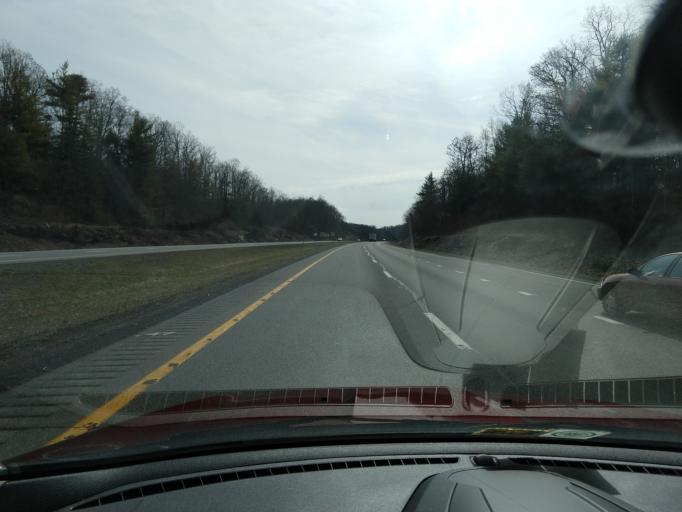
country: US
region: West Virginia
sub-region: Greenbrier County
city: Lewisburg
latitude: 37.8127
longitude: -80.4187
